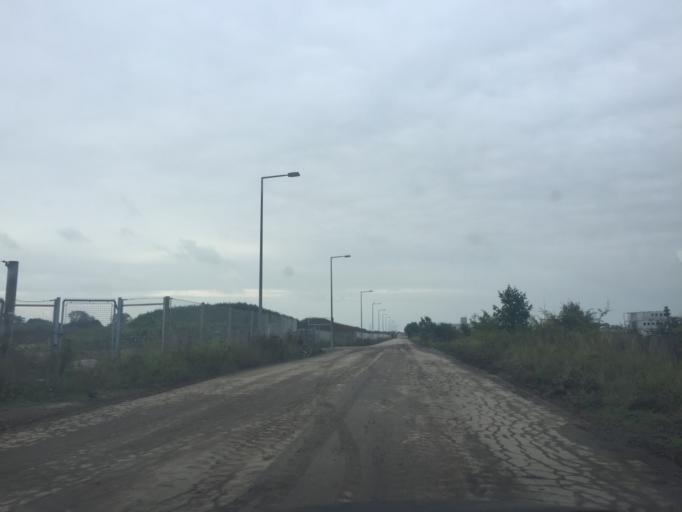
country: DK
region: Capital Region
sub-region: Hoje-Taastrup Kommune
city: Flong
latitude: 55.6466
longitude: 12.1970
